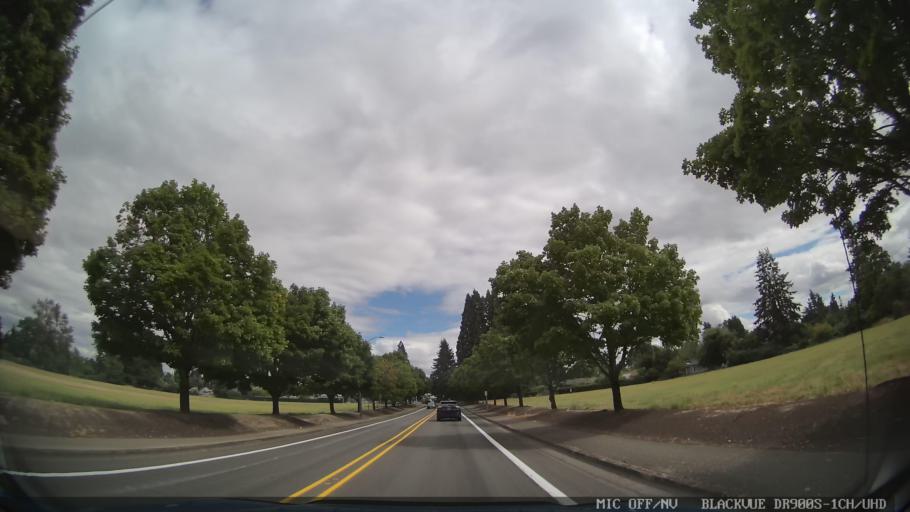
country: US
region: Oregon
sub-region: Marion County
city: Salem
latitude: 44.9551
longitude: -123.0060
